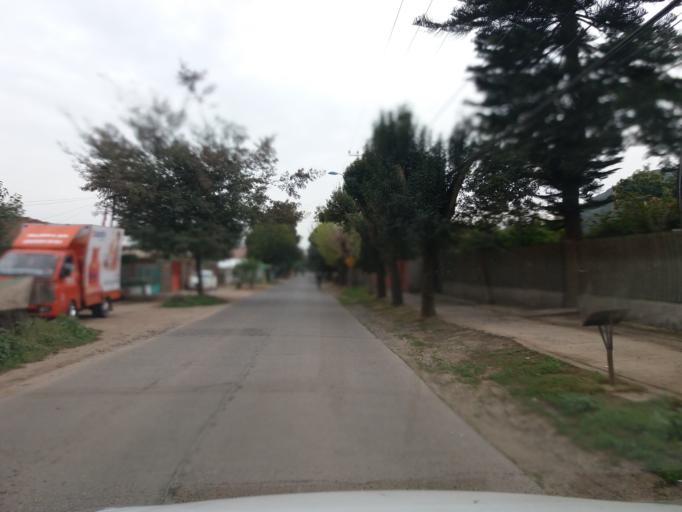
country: CL
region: Valparaiso
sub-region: Provincia de Quillota
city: Hacienda La Calera
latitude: -32.8147
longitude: -71.1381
